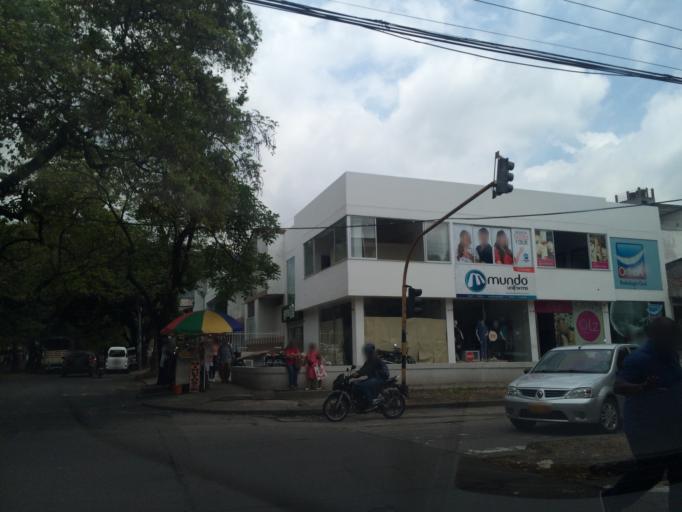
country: CO
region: Valle del Cauca
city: Cali
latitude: 3.4209
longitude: -76.5445
